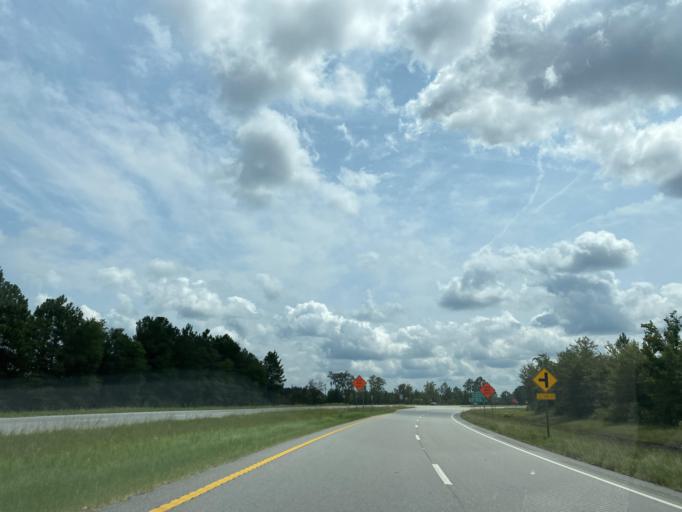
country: US
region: Georgia
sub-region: Ware County
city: Deenwood
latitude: 31.2473
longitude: -82.4284
